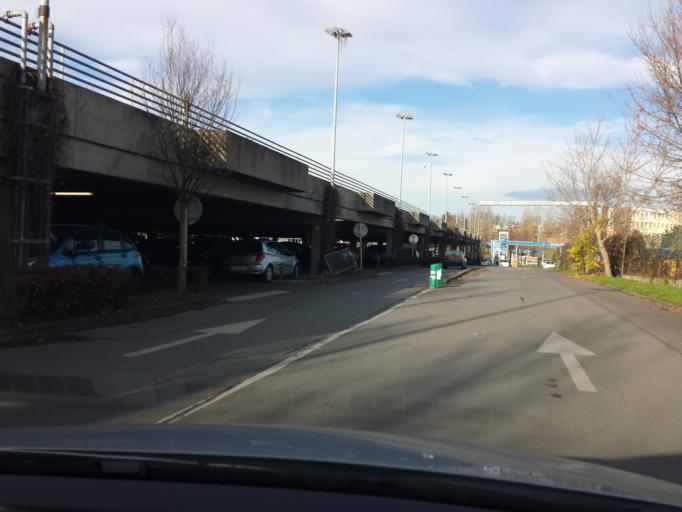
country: FR
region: Ile-de-France
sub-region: Departement de l'Essonne
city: Massy
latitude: 48.7253
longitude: 2.2798
